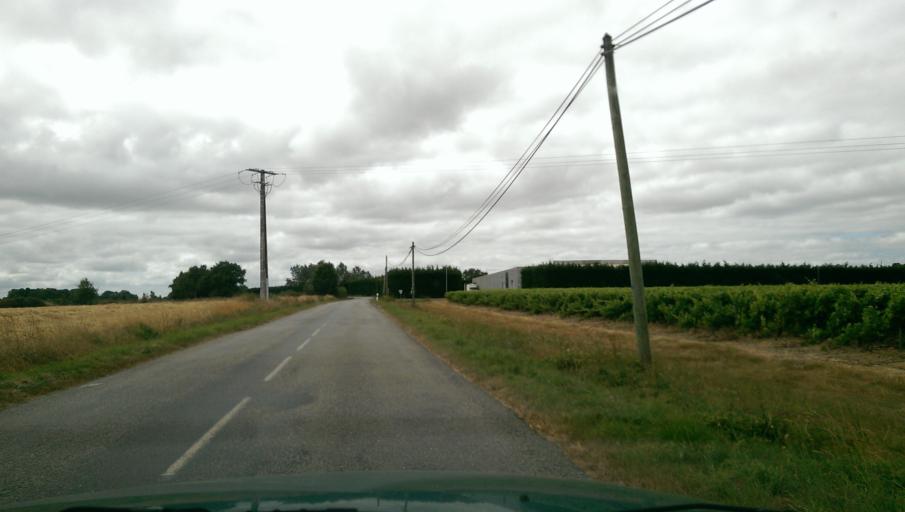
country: FR
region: Pays de la Loire
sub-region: Departement de la Loire-Atlantique
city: Remouille
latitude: 47.0485
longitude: -1.3893
